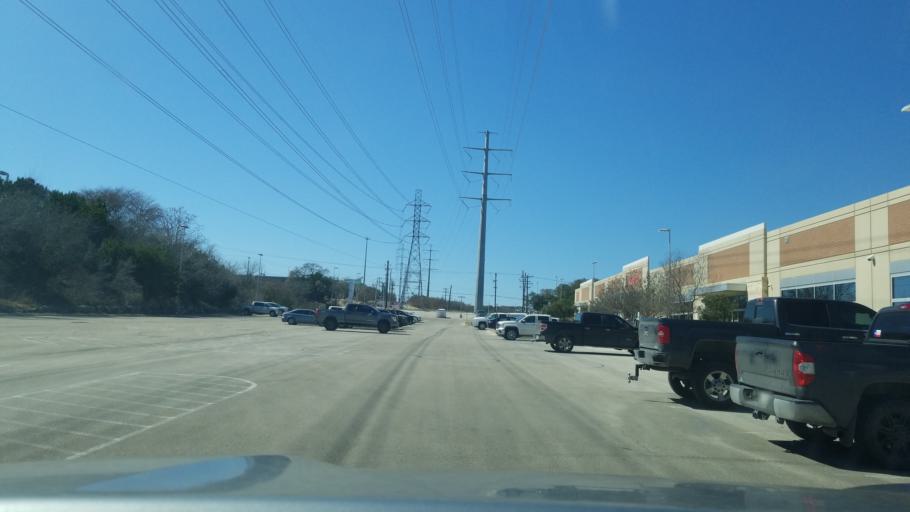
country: US
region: Texas
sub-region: Bexar County
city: Hollywood Park
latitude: 29.6153
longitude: -98.4639
